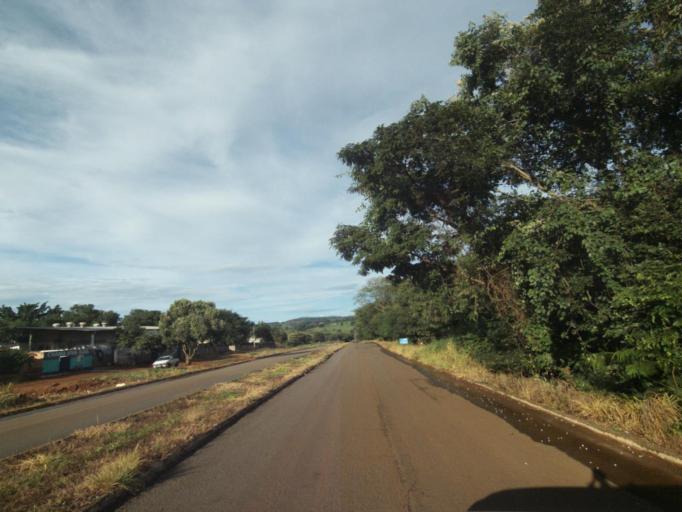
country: BR
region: Goias
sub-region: Itaberai
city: Itaberai
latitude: -15.9203
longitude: -49.5992
